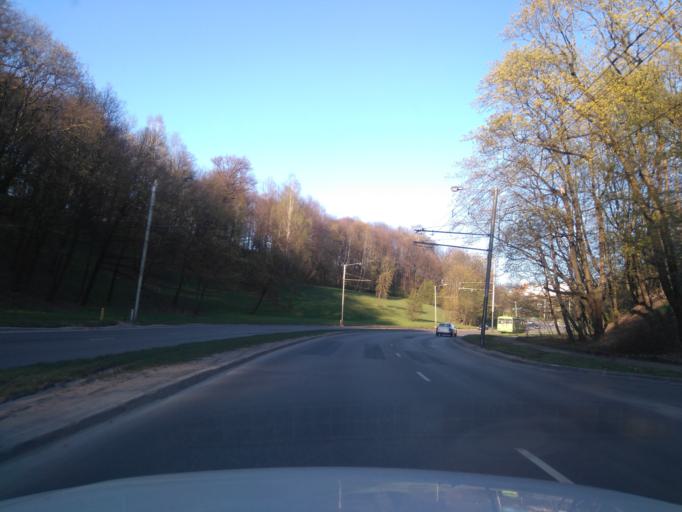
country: LT
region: Kauno apskritis
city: Dainava (Kaunas)
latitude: 54.8954
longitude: 23.9444
